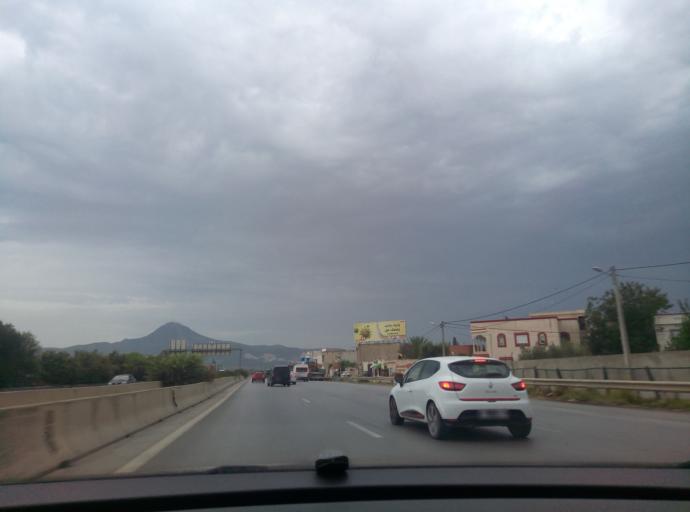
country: TN
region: Tunis
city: La Sebala du Mornag
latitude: 36.7148
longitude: 10.2746
